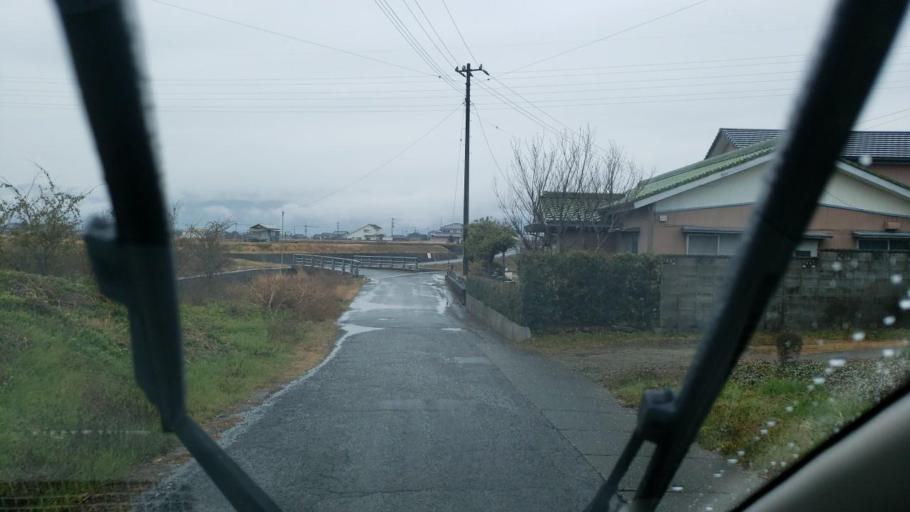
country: JP
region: Tokushima
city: Kamojimacho-jogejima
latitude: 34.0843
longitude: 134.2559
